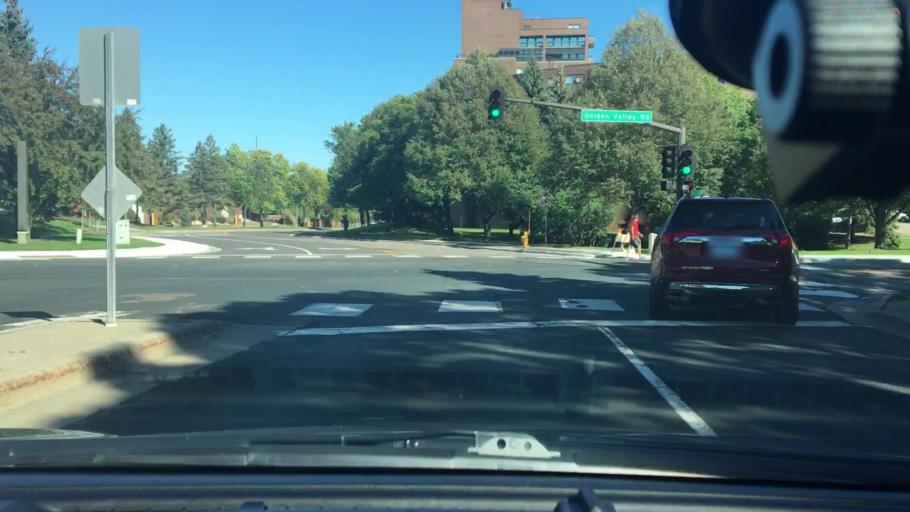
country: US
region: Minnesota
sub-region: Hennepin County
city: Golden Valley
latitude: 44.9859
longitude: -93.3772
